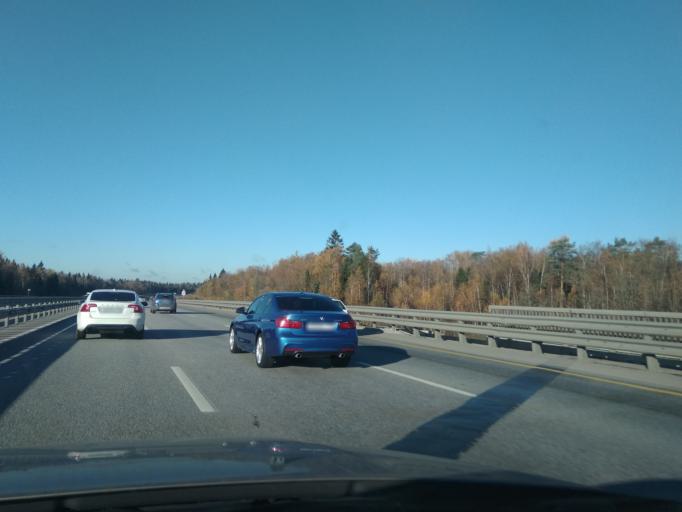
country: RU
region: Moskovskaya
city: Yershovo
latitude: 55.8294
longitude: 36.8720
